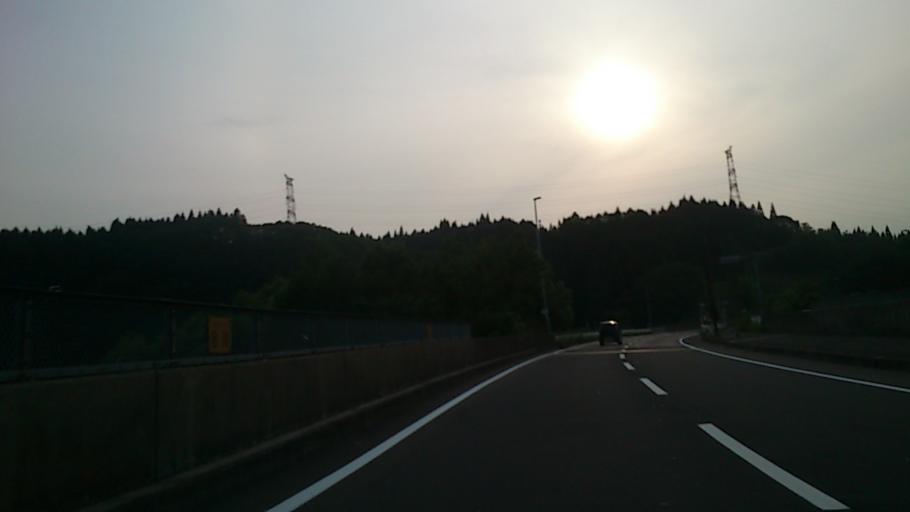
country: JP
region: Akita
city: Takanosu
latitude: 40.2083
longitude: 140.2038
